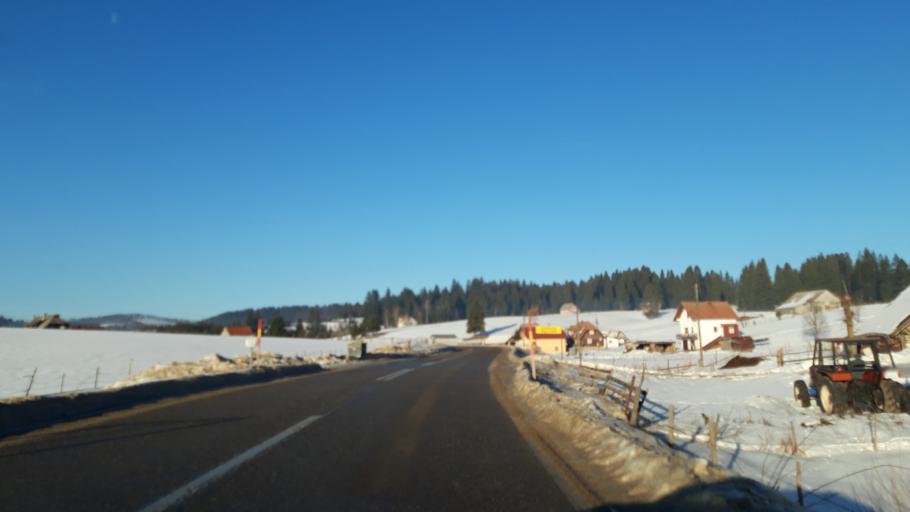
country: BA
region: Republika Srpska
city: Han Pijesak
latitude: 44.1055
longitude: 18.9701
